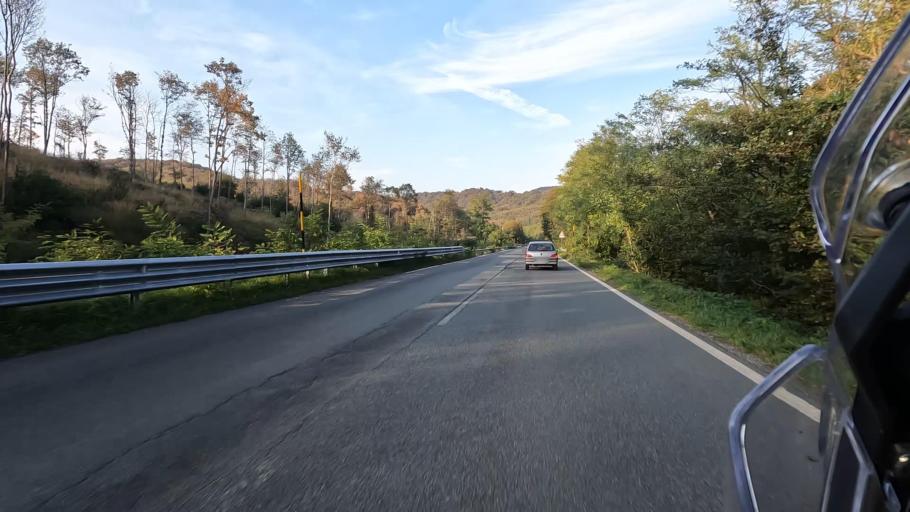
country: IT
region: Liguria
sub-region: Provincia di Savona
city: Osteria dei Cacciatori-Stella
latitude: 44.4377
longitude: 8.4824
